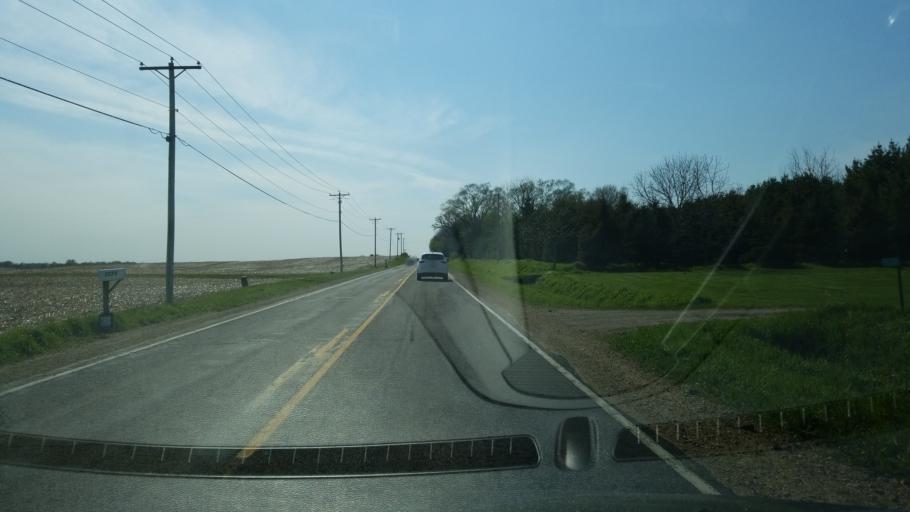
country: US
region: Wisconsin
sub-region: Dane County
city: Oregon
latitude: 42.9291
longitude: -89.4151
